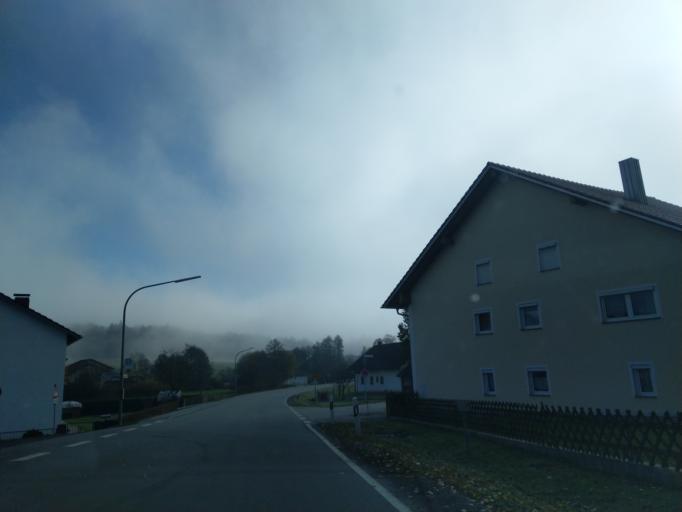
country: DE
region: Bavaria
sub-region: Lower Bavaria
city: Schollnach
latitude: 48.7323
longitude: 13.1704
